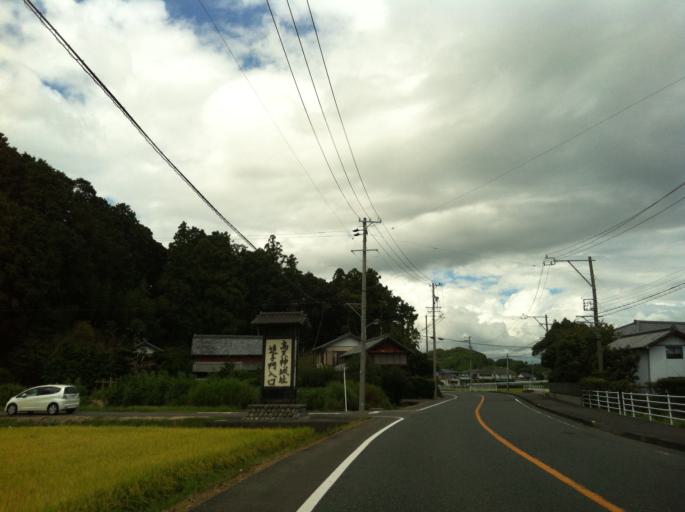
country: JP
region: Shizuoka
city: Kakegawa
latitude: 34.6985
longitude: 138.0451
